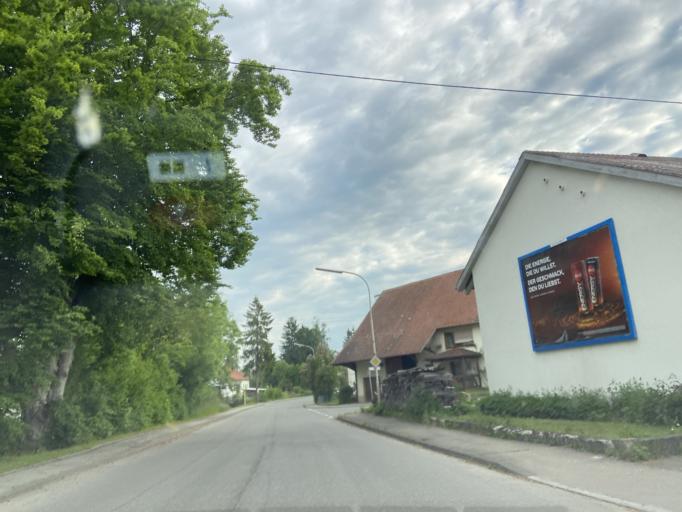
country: DE
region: Baden-Wuerttemberg
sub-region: Tuebingen Region
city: Hohentengen
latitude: 48.0349
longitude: 9.3704
